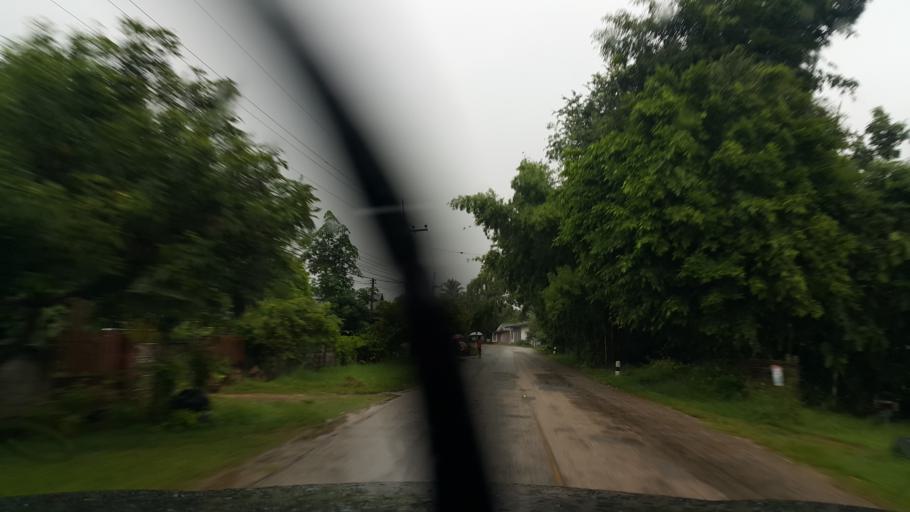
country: TH
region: Phayao
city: Phu Sang
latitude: 19.5886
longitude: 100.3696
